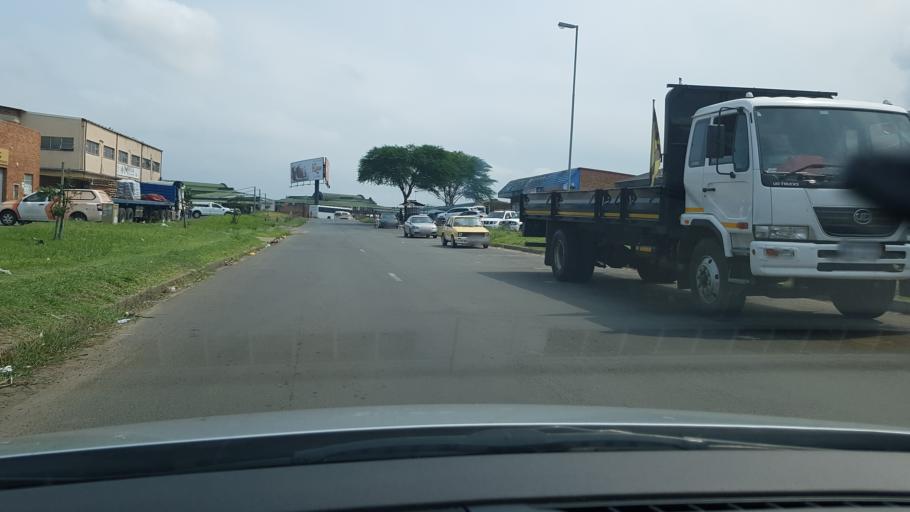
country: ZA
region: KwaZulu-Natal
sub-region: uThungulu District Municipality
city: Richards Bay
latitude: -28.7476
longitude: 32.0486
